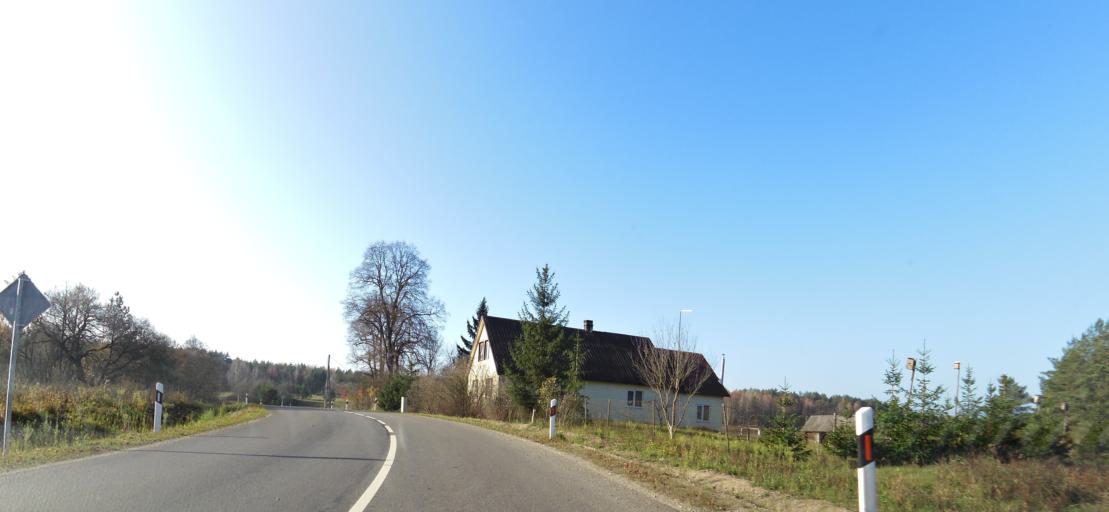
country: LT
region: Vilnius County
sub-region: Trakai
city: Rudiskes
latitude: 54.5103
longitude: 24.8774
